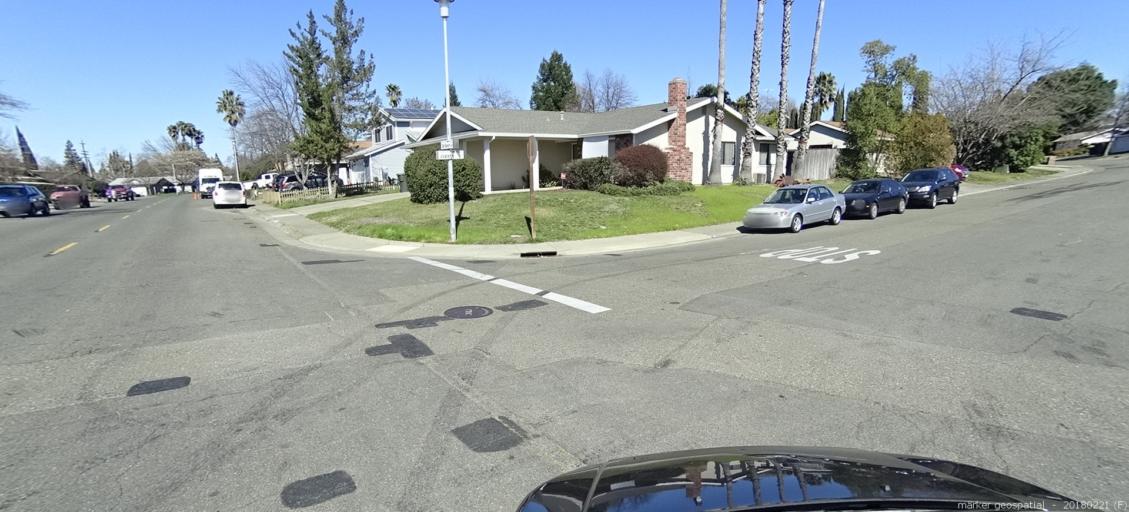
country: US
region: California
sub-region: Sacramento County
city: Orangevale
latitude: 38.6918
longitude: -121.2492
